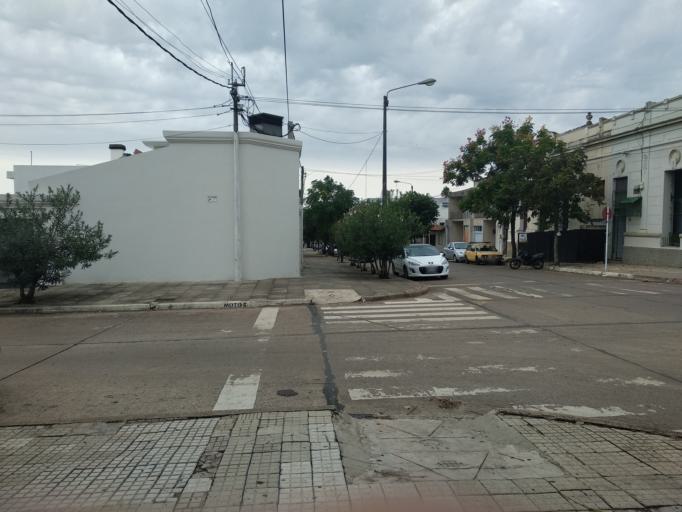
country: UY
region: Artigas
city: Artigas
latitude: -30.4012
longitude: -56.4675
